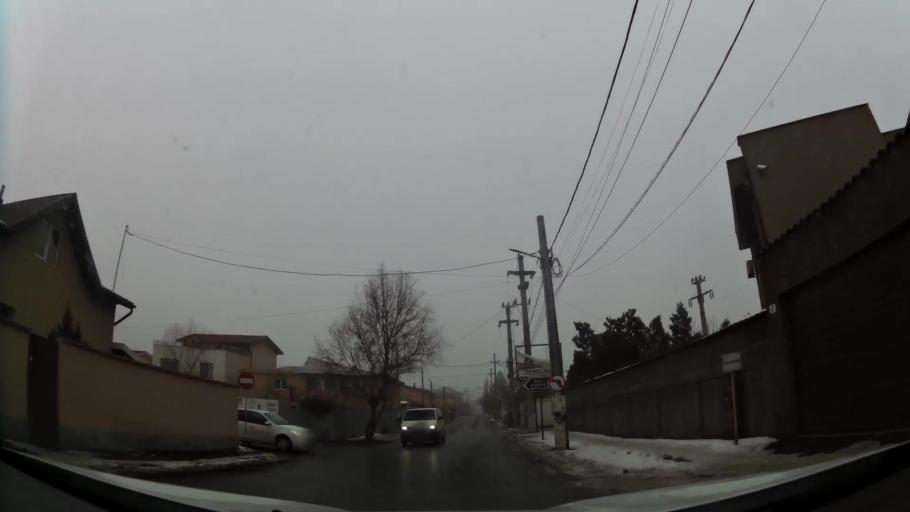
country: RO
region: Ilfov
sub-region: Comuna Chiajna
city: Rosu
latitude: 44.4438
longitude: 26.0119
